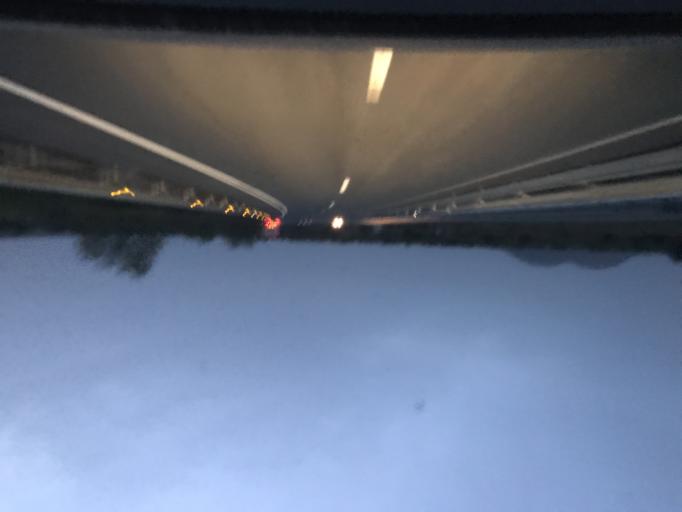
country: ES
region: Andalusia
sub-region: Provincia de Granada
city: Gor
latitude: 37.4024
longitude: -2.9279
